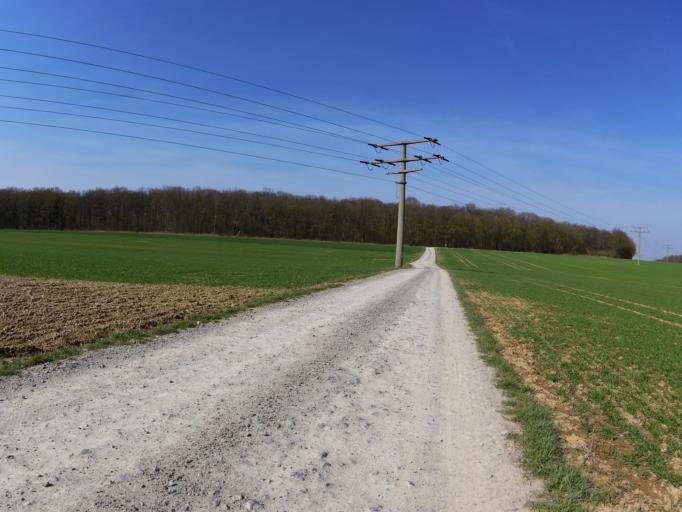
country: DE
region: Bavaria
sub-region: Regierungsbezirk Unterfranken
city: Rottendorf
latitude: 49.8071
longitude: 10.0266
